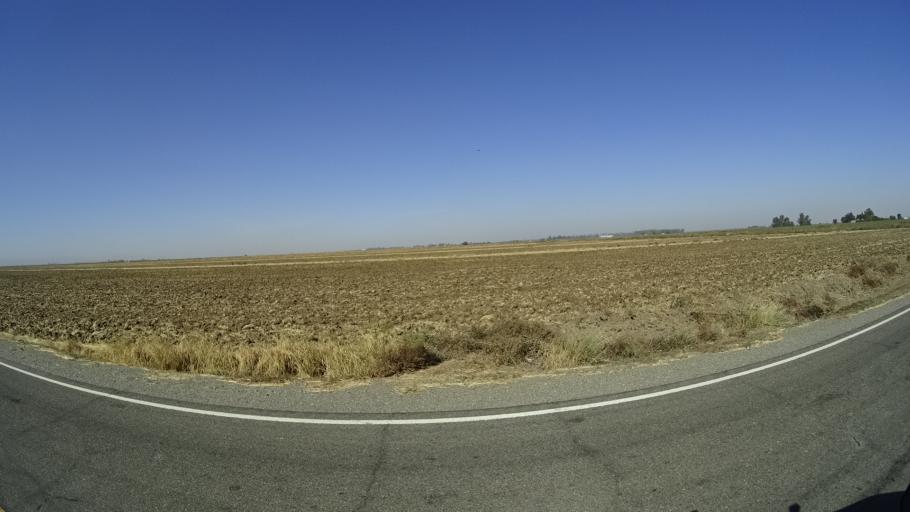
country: US
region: California
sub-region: Yolo County
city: Winters
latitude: 38.5907
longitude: -121.8877
